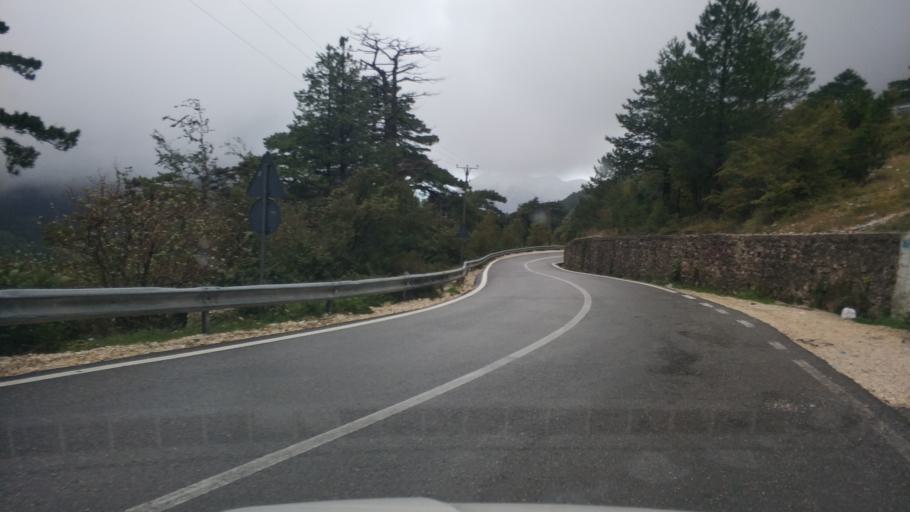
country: AL
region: Vlore
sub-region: Rrethi i Vlores
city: Vranisht
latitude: 40.2033
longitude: 19.5876
